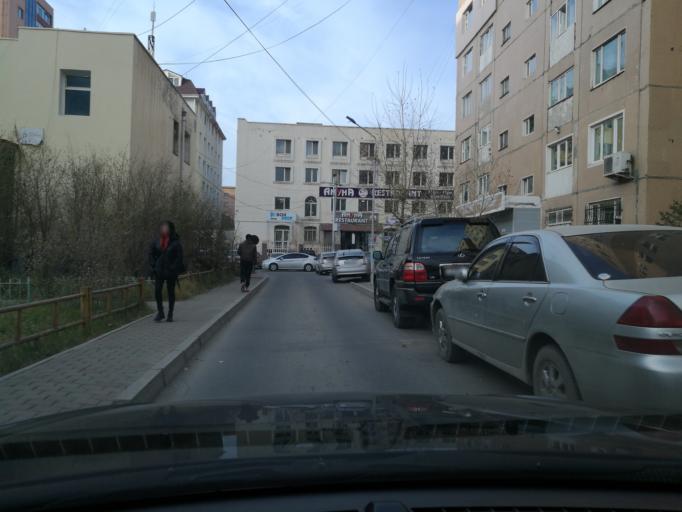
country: MN
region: Ulaanbaatar
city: Ulaanbaatar
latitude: 47.9277
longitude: 106.9262
